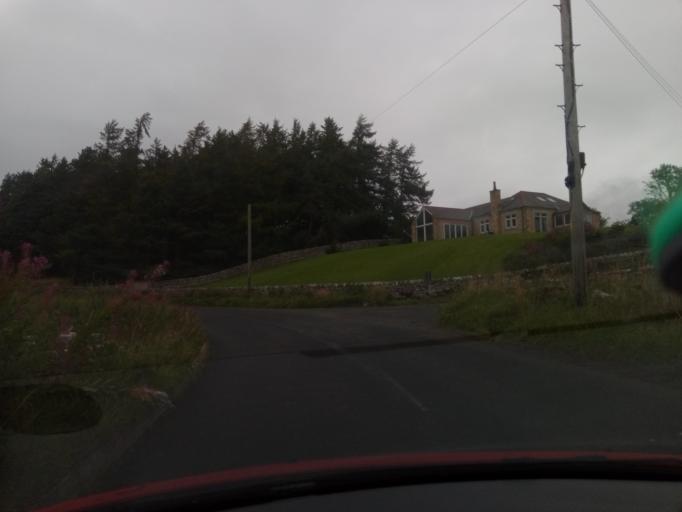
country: GB
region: England
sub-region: Northumberland
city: Rothley
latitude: 55.1872
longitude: -1.9369
